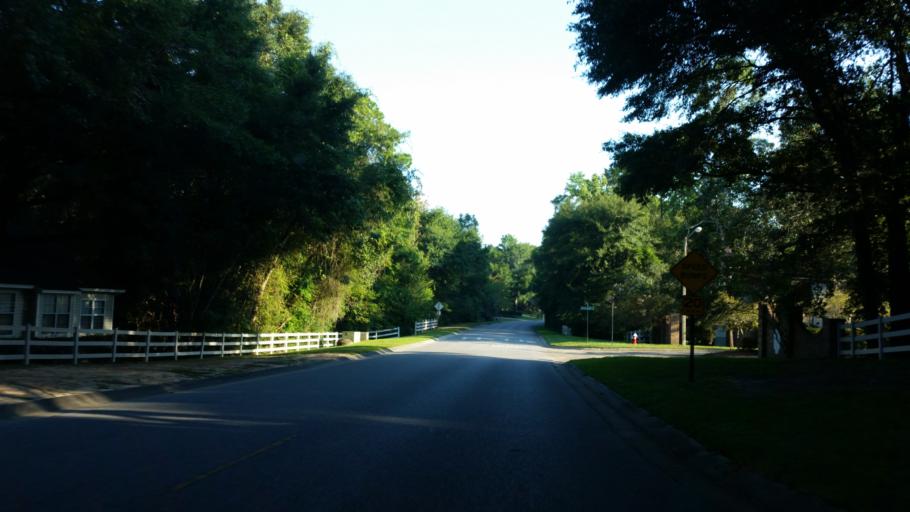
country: US
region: Florida
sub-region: Escambia County
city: Ensley
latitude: 30.5430
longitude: -87.2393
